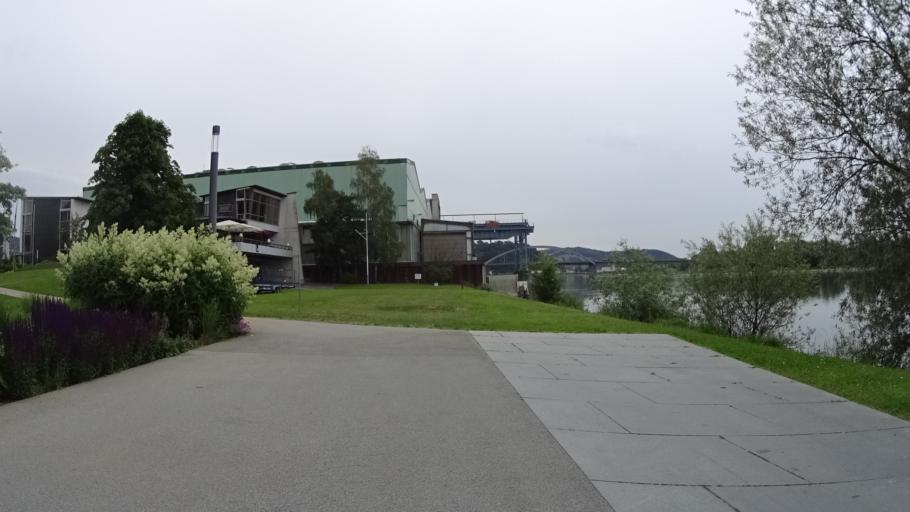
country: DE
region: Bavaria
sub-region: Lower Bavaria
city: Deggendorf
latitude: 48.8277
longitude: 12.9546
